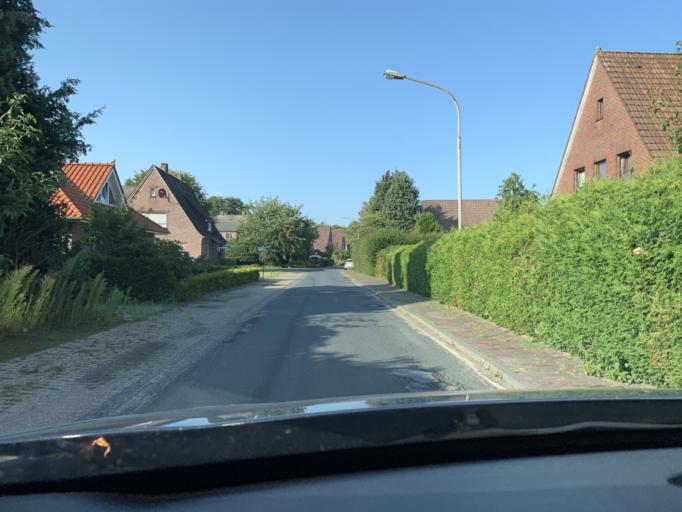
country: DE
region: Lower Saxony
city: Westerstede
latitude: 53.2627
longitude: 7.9307
